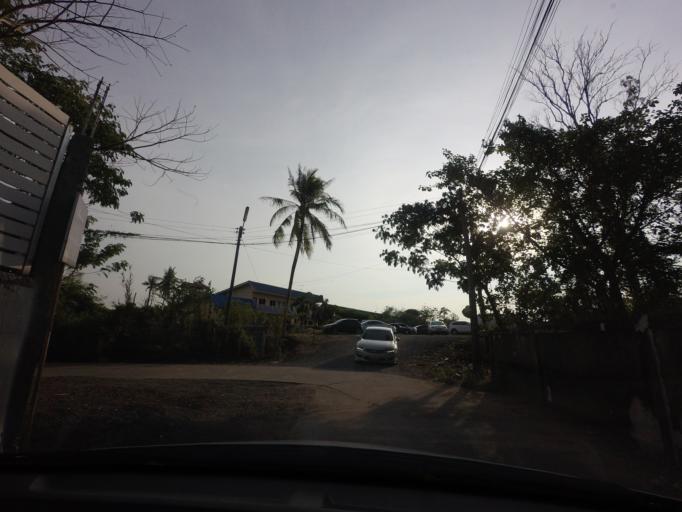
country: TH
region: Pathum Thani
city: Sam Khok
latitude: 14.0455
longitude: 100.5523
